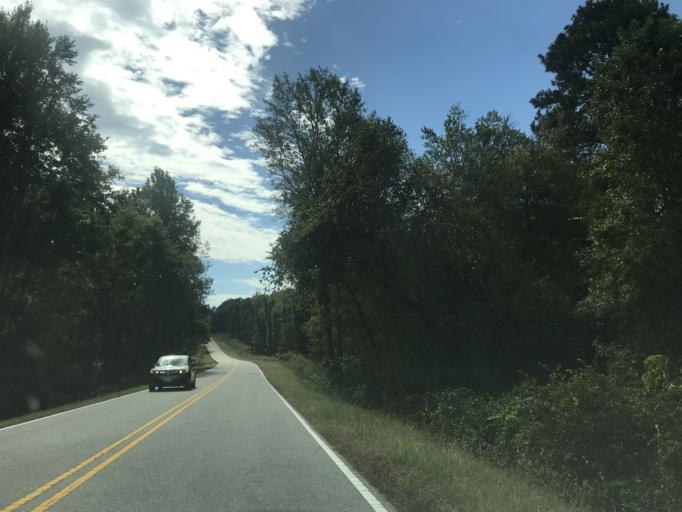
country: US
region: North Carolina
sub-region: Wake County
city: Rolesville
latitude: 35.8778
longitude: -78.4756
